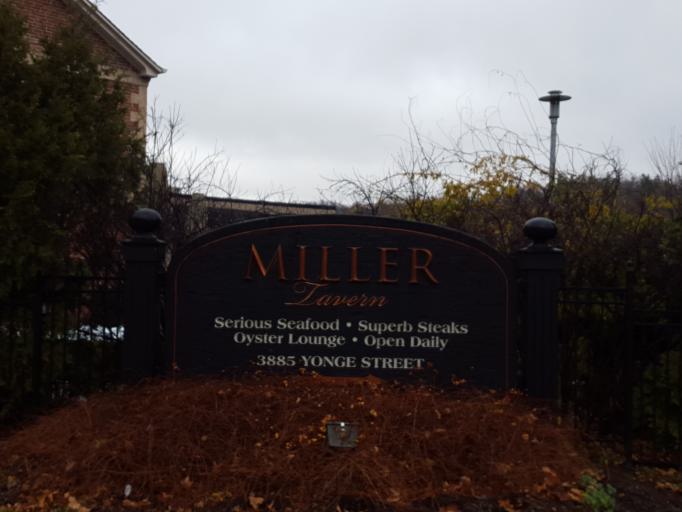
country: CA
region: Ontario
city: Willowdale
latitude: 43.7407
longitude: -79.4059
